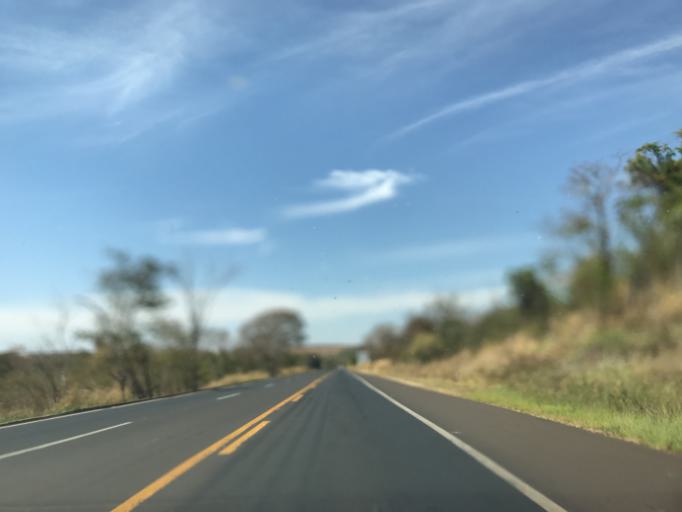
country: BR
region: Minas Gerais
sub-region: Monte Alegre De Minas
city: Monte Alegre de Minas
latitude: -18.9322
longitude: -49.0308
